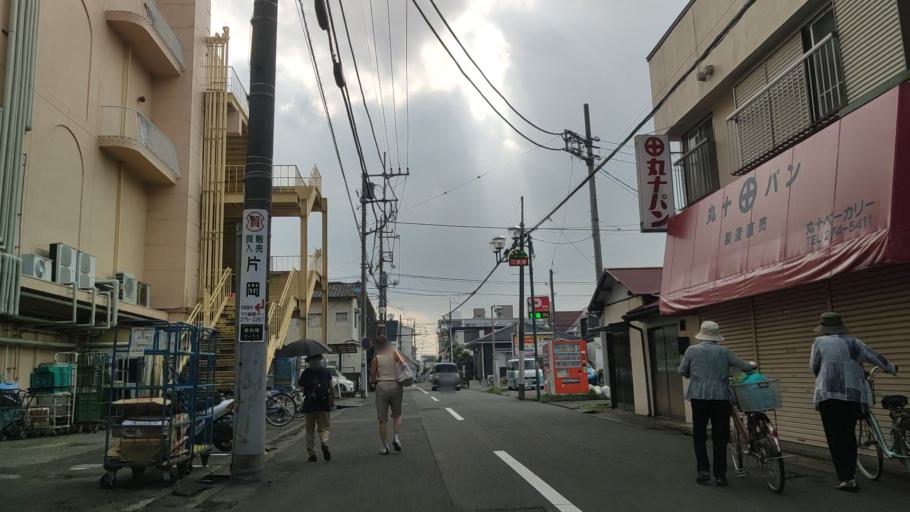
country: JP
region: Kanagawa
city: Minami-rinkan
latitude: 35.4943
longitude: 139.4469
